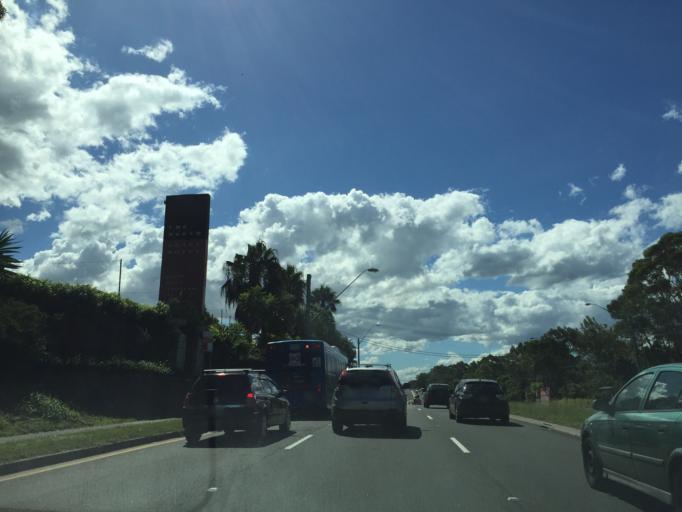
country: AU
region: New South Wales
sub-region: Ryde
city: Macquarie Park
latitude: -33.7814
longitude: 151.1132
